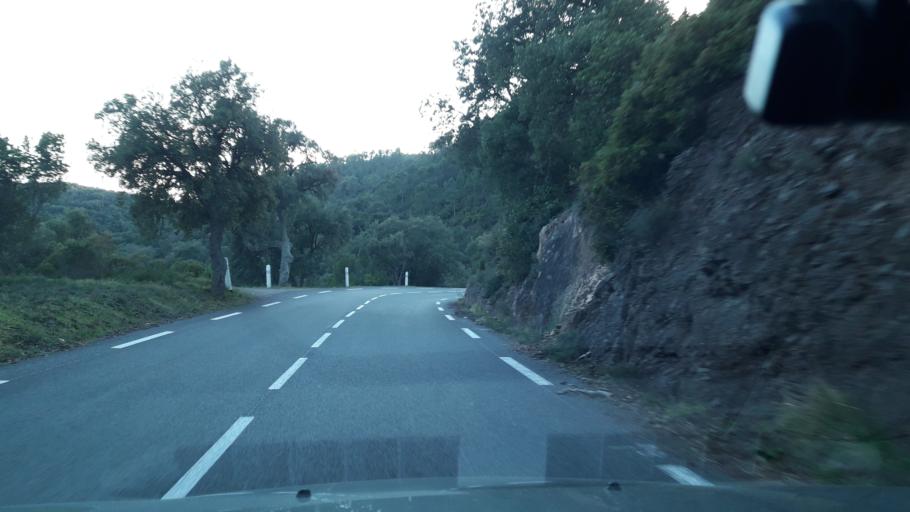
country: FR
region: Provence-Alpes-Cote d'Azur
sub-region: Departement du Var
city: Saint-Raphael
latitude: 43.4881
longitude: 6.7769
